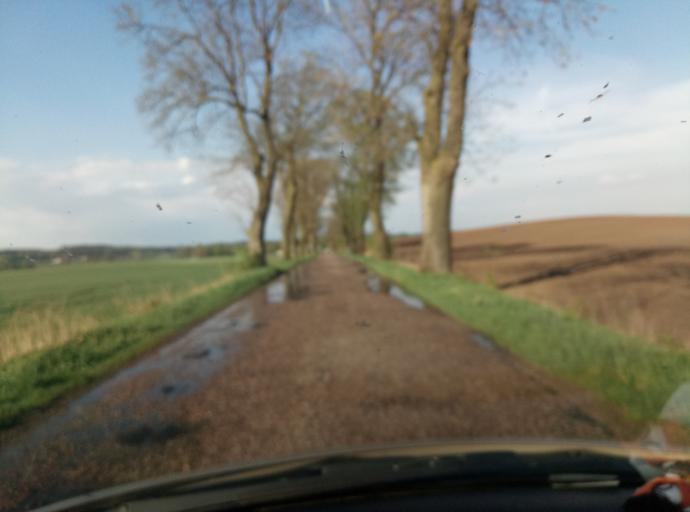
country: PL
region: Warmian-Masurian Voivodeship
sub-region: Powiat nowomiejski
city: Biskupiec
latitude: 53.4370
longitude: 19.2806
